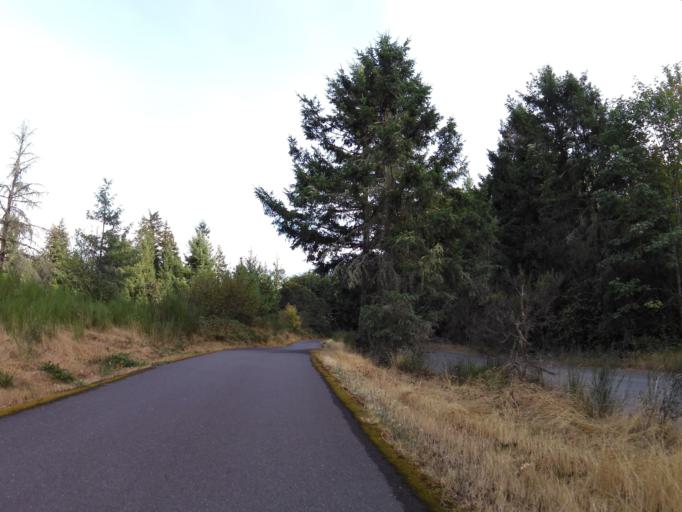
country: US
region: Washington
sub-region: Thurston County
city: Tenino
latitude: 46.9200
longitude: -122.8020
